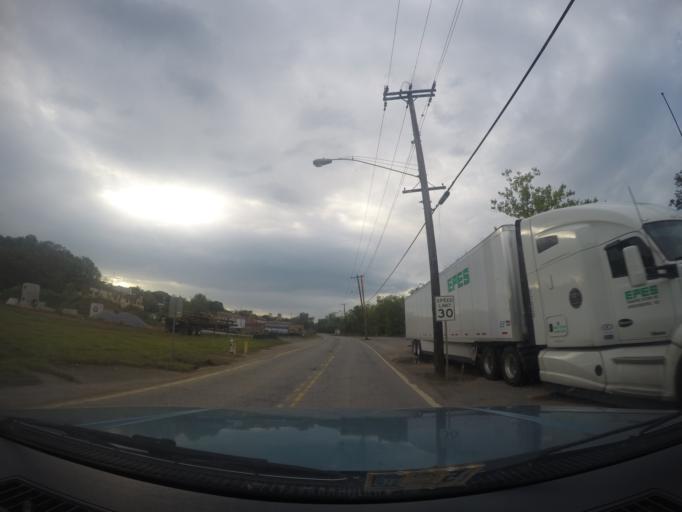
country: US
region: Virginia
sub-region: City of Lynchburg
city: Lynchburg
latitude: 37.4059
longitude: -79.1300
